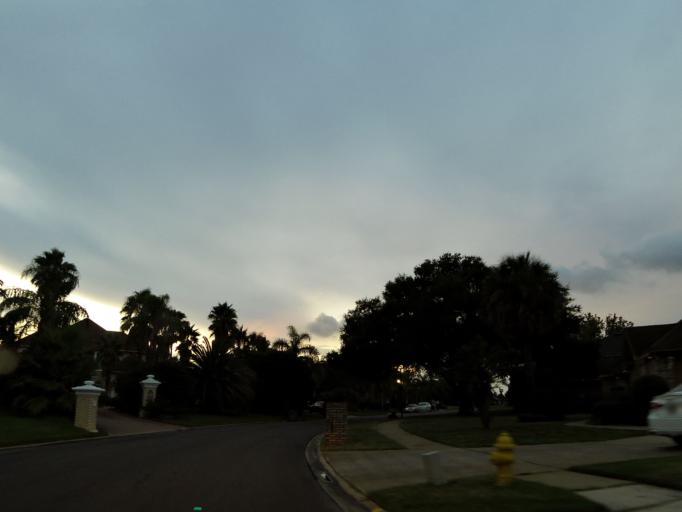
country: US
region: Florida
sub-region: Duval County
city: Jacksonville
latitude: 30.3832
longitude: -81.6210
